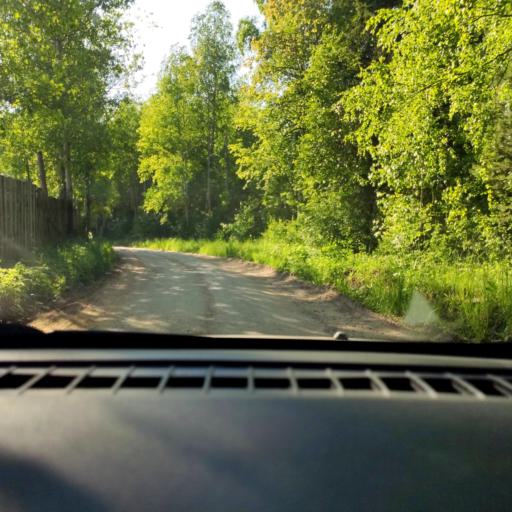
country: RU
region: Perm
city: Overyata
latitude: 58.1241
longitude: 55.8727
